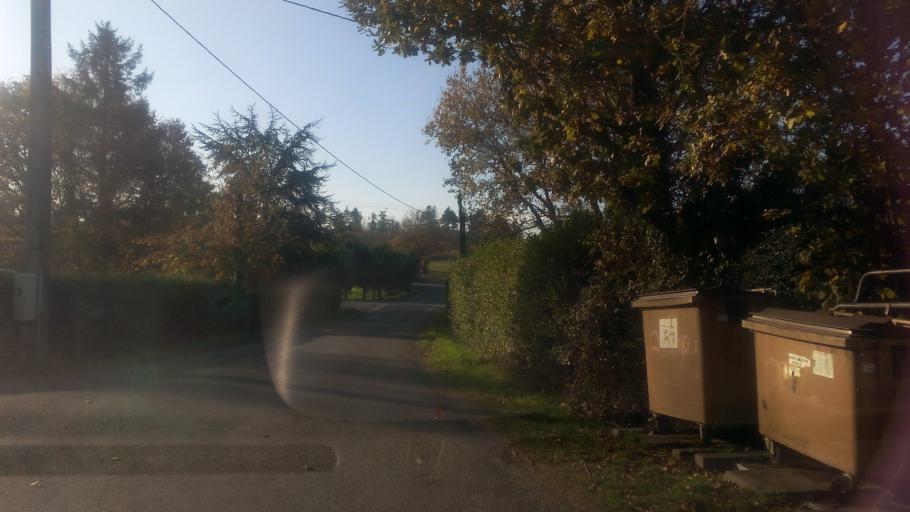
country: FR
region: Pays de la Loire
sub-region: Departement de la Loire-Atlantique
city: Avessac
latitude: 47.6562
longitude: -1.9935
